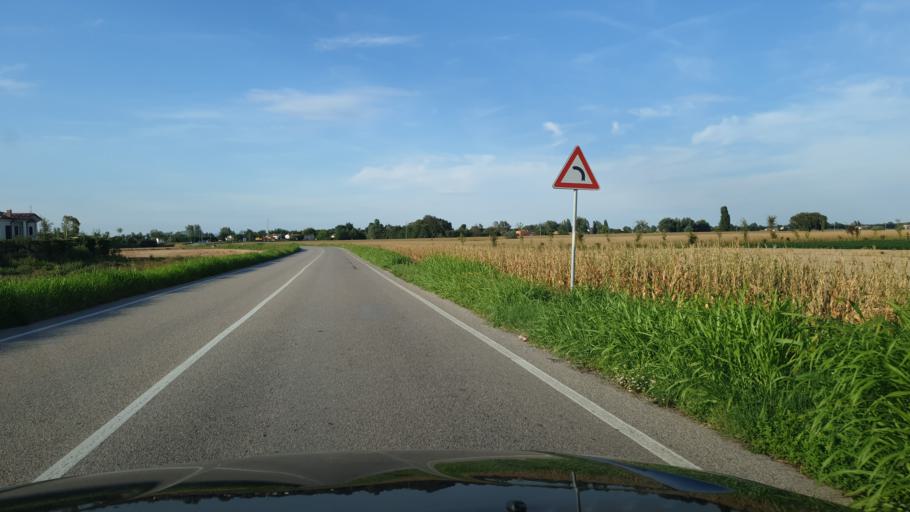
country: IT
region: Veneto
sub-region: Provincia di Rovigo
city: Pincara
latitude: 44.9936
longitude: 11.6154
